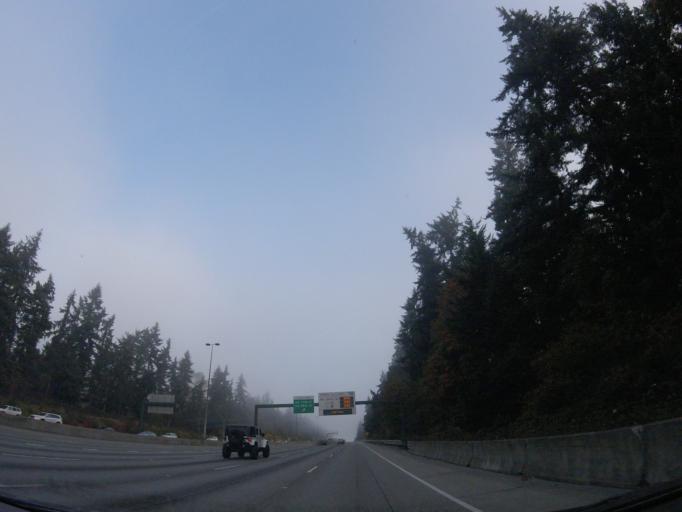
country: US
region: Washington
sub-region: King County
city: Yarrow Point
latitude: 47.6460
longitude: -122.1867
